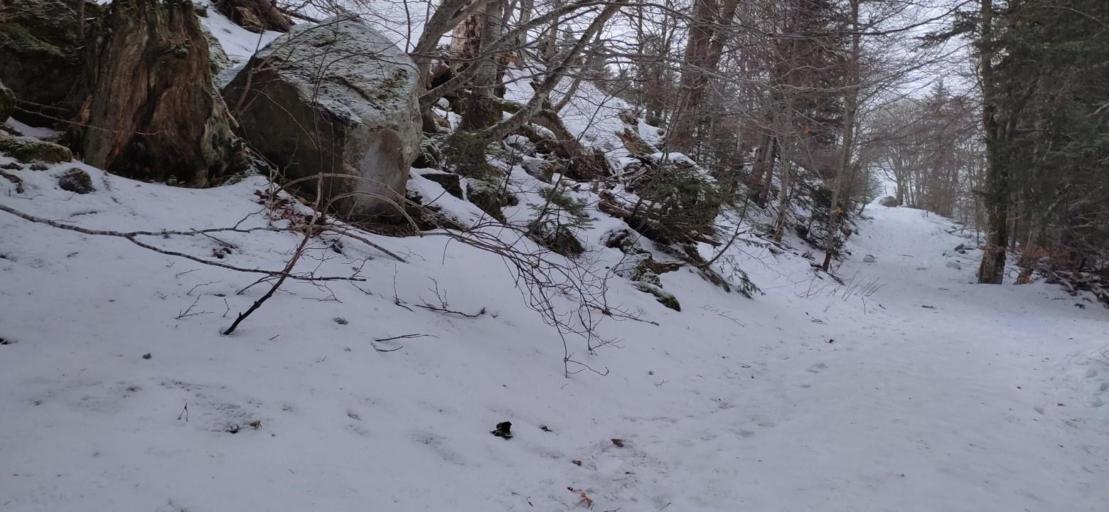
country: FR
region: Auvergne
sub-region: Departement du Puy-de-Dome
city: Mont-Dore
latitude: 45.5491
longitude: 2.8152
